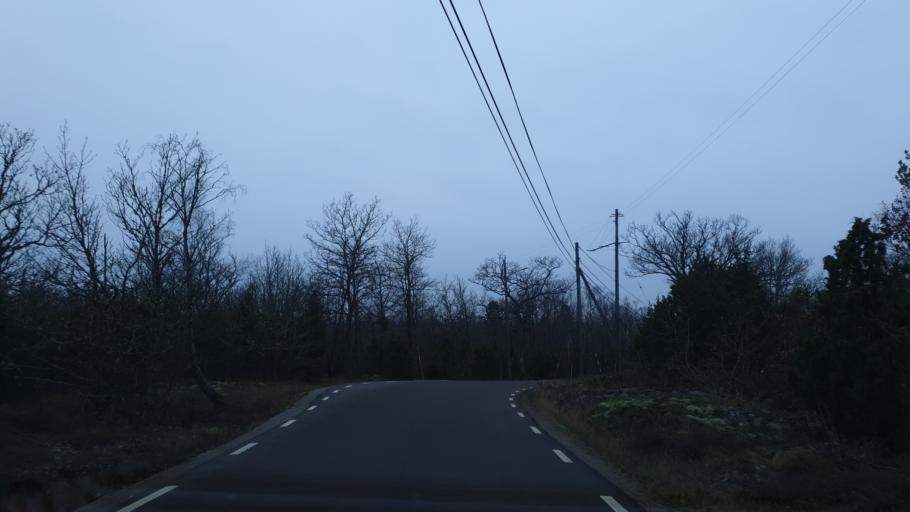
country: SE
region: Blekinge
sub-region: Karlskrona Kommun
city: Karlskrona
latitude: 56.1178
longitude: 15.6186
